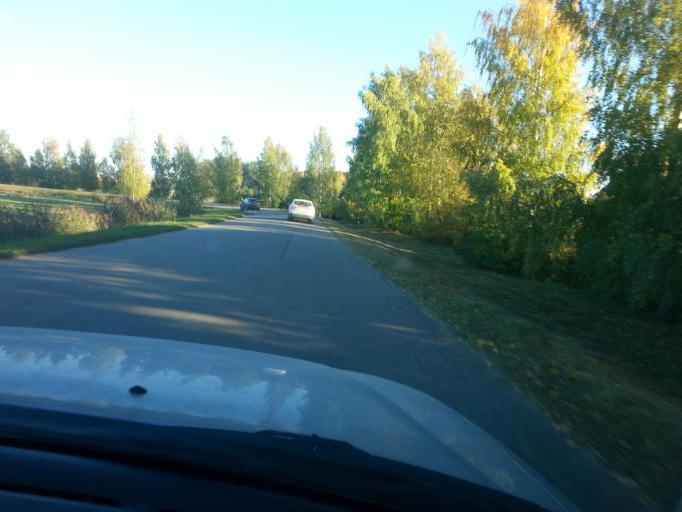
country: LV
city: Tervete
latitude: 56.6172
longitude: 23.4509
